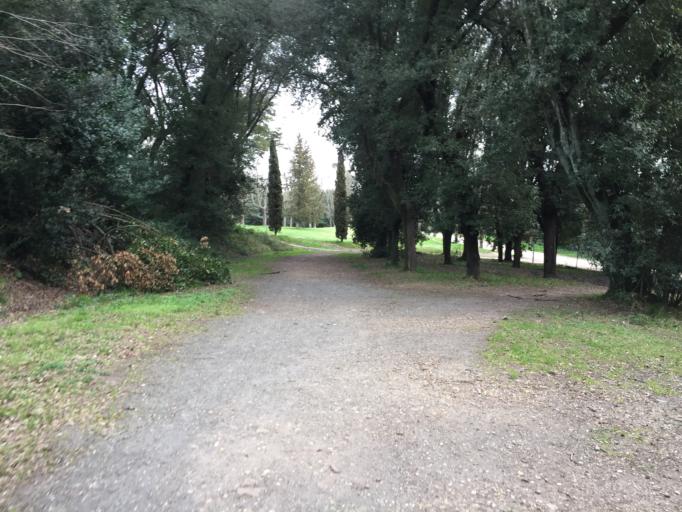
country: VA
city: Vatican City
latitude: 41.8833
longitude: 12.4463
